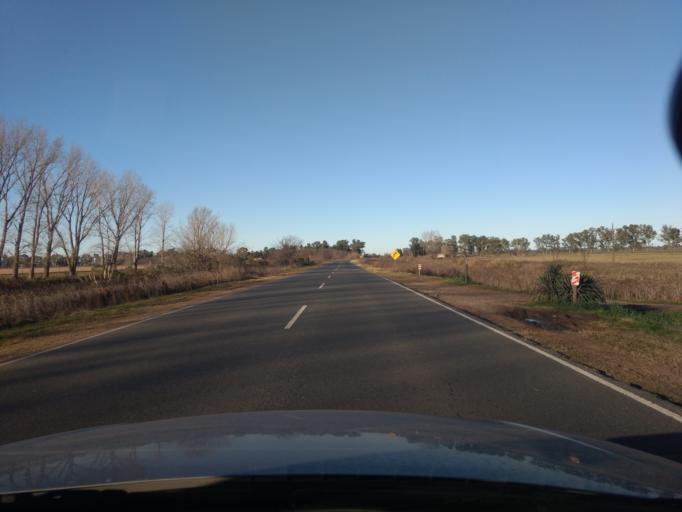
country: AR
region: Buenos Aires
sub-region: Partido de Lujan
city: Lujan
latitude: -34.6197
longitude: -59.1071
